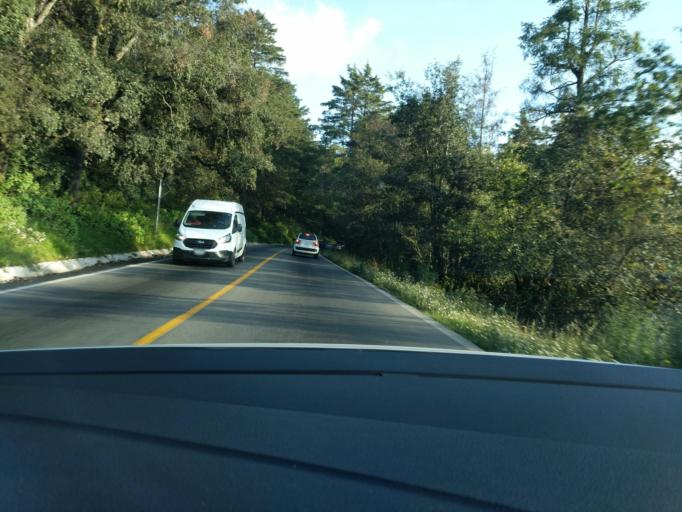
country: MX
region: Hidalgo
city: Mineral del Monte
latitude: 20.1464
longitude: -98.6852
